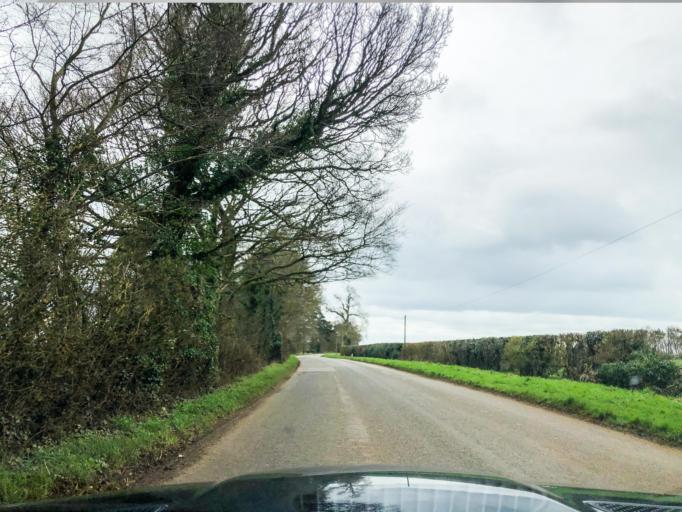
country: GB
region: England
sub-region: Oxfordshire
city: Hanwell
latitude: 52.1057
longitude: -1.4749
